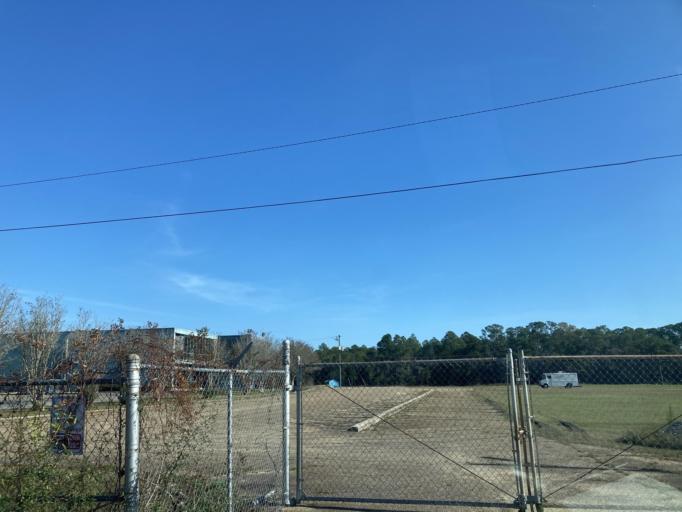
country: US
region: Mississippi
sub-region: Harrison County
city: West Gulfport
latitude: 30.3903
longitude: -89.0867
